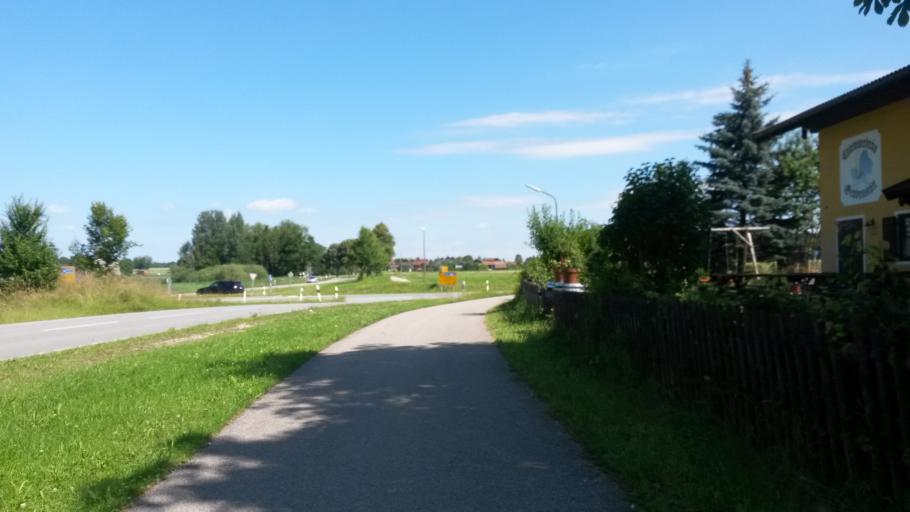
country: DE
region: Bavaria
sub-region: Upper Bavaria
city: Grabenstatt
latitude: 47.8505
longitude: 12.5416
